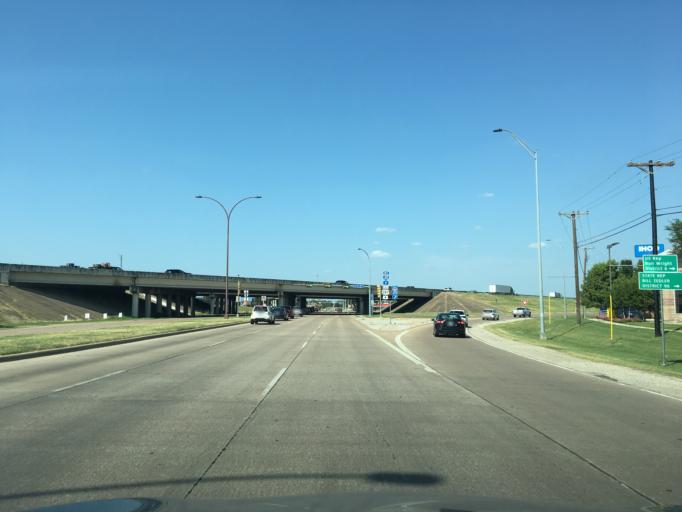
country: US
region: Texas
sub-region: Tarrant County
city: Kennedale
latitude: 32.6719
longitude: -97.2012
